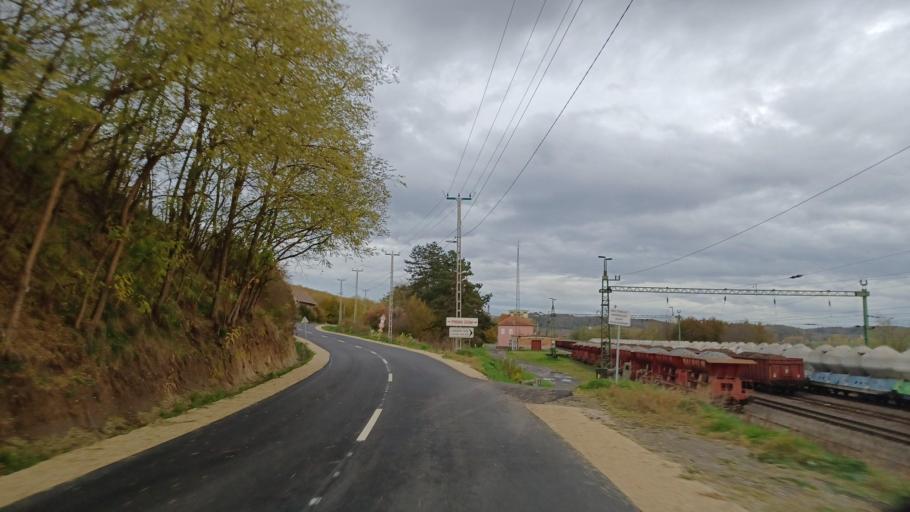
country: HU
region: Tolna
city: Gyonk
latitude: 46.5992
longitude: 18.4252
